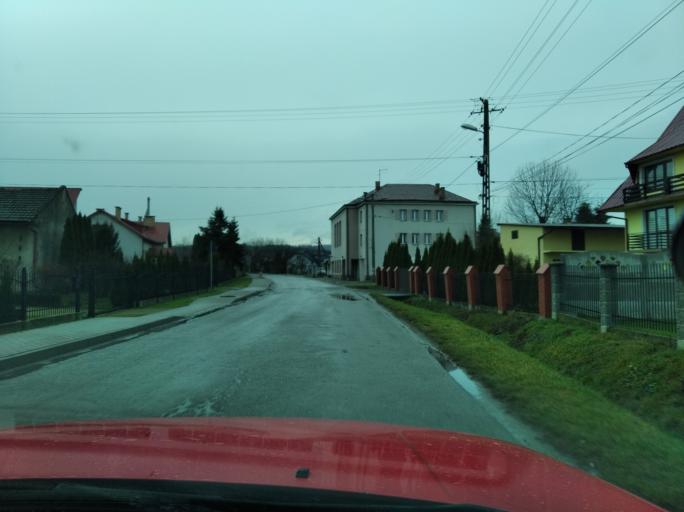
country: PL
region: Subcarpathian Voivodeship
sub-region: Powiat rzeszowski
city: Lutoryz
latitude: 49.9513
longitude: 21.9255
